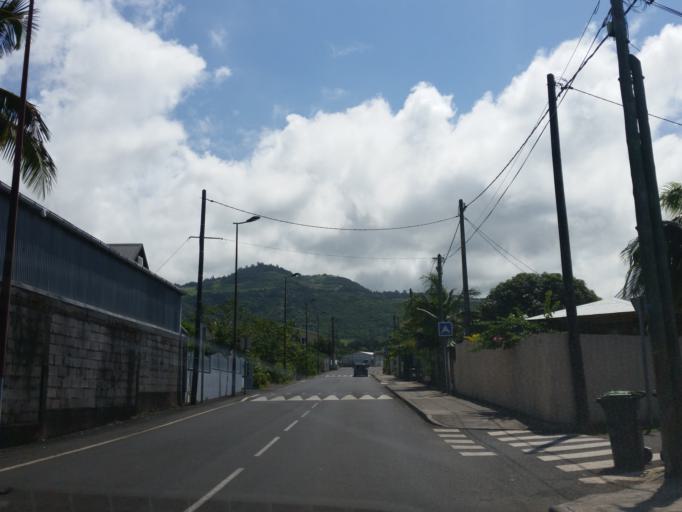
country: RE
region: Reunion
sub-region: Reunion
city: Saint-Joseph
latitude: -21.3801
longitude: 55.6098
